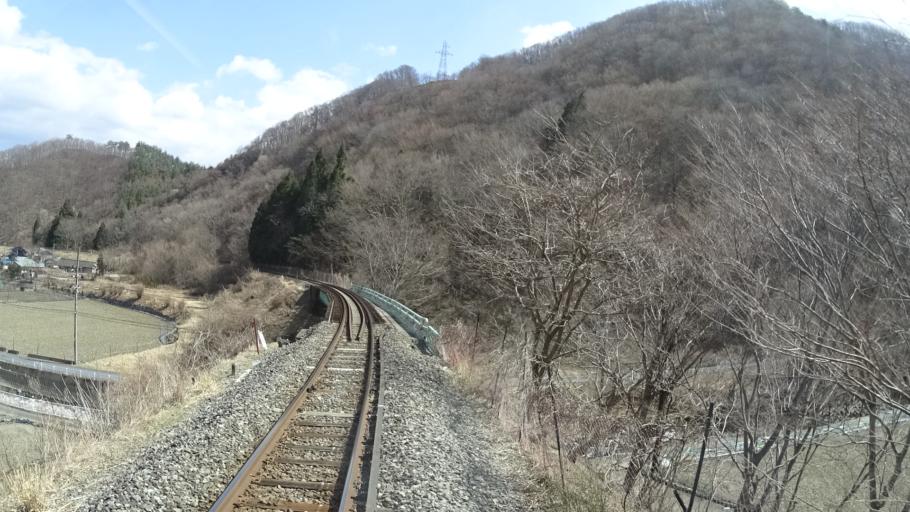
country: JP
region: Iwate
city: Kamaishi
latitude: 39.2518
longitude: 141.7392
